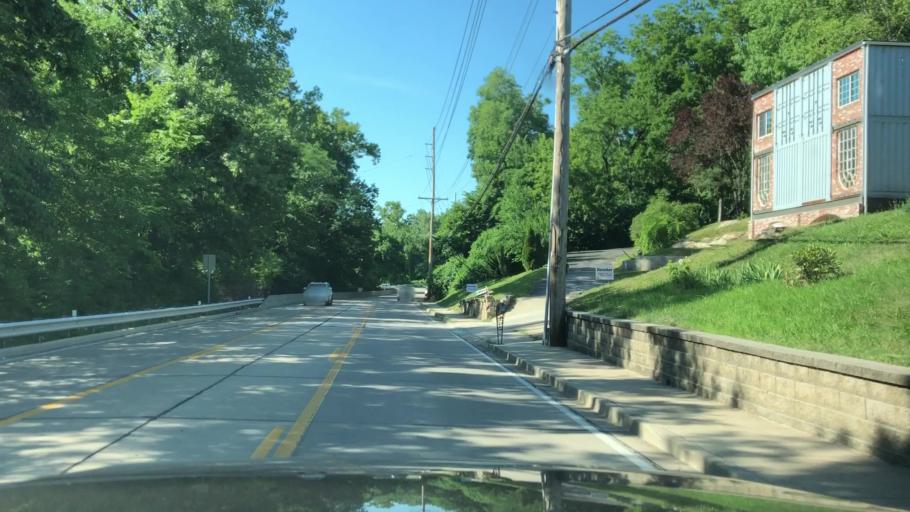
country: US
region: Missouri
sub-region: Saint Charles County
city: Saint Charles
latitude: 38.8107
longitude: -90.5128
